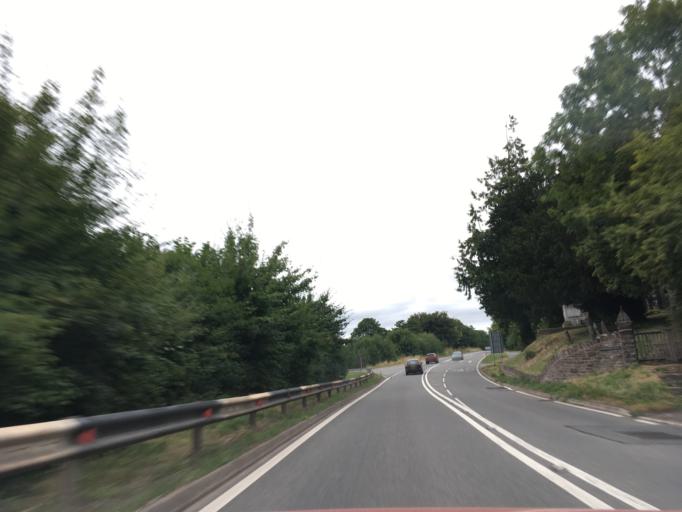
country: GB
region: Wales
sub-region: Sir Powys
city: Brecon
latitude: 51.9023
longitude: -3.2767
